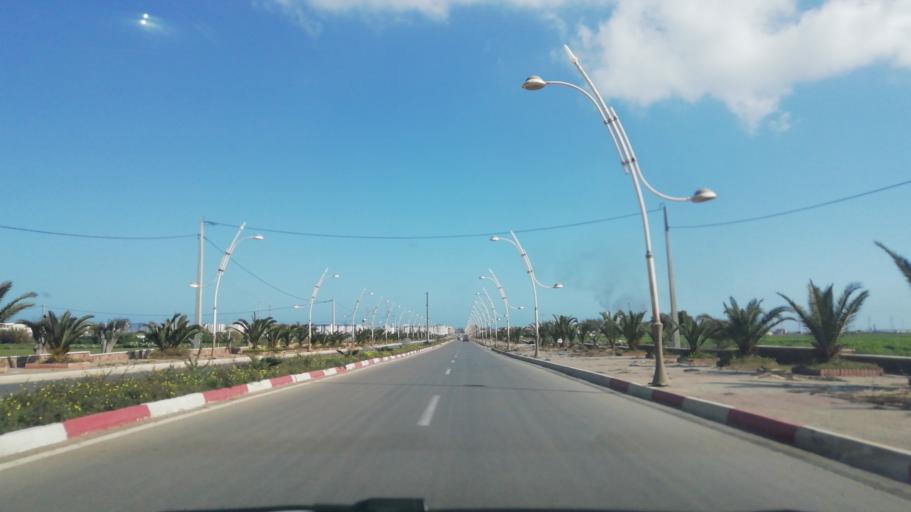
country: DZ
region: Oran
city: Ain el Bya
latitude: 35.7893
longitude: -0.2816
